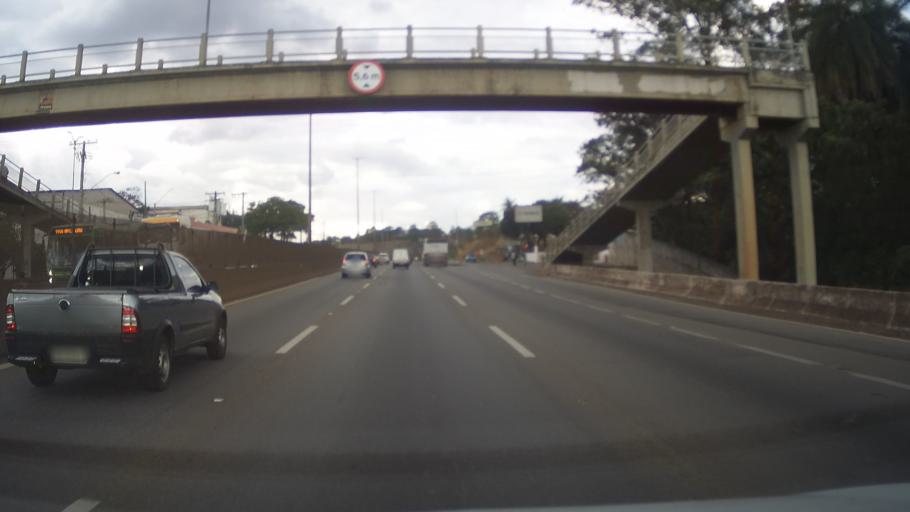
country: BR
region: Minas Gerais
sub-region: Betim
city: Betim
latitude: -19.9566
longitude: -44.1266
